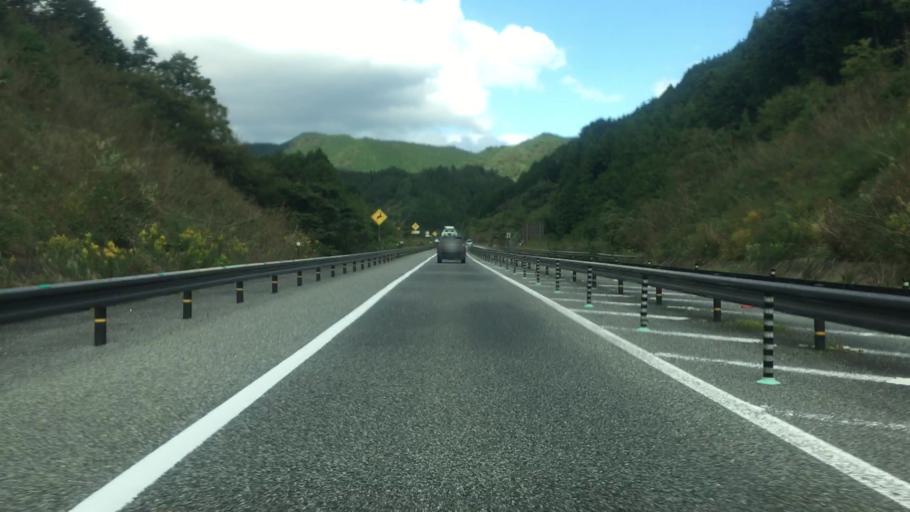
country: JP
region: Kyoto
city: Fukuchiyama
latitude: 35.2531
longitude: 135.0126
